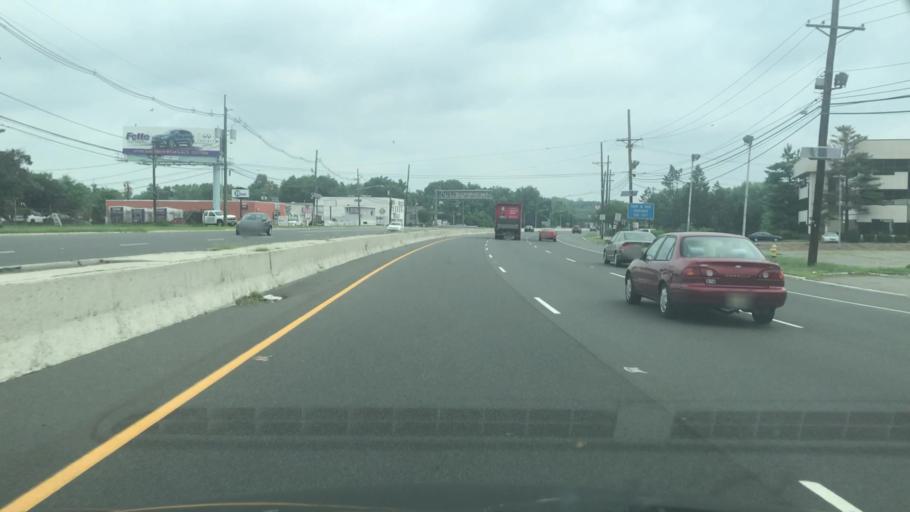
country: US
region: New Jersey
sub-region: Passaic County
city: Wayne
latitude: 40.9201
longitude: -74.2675
